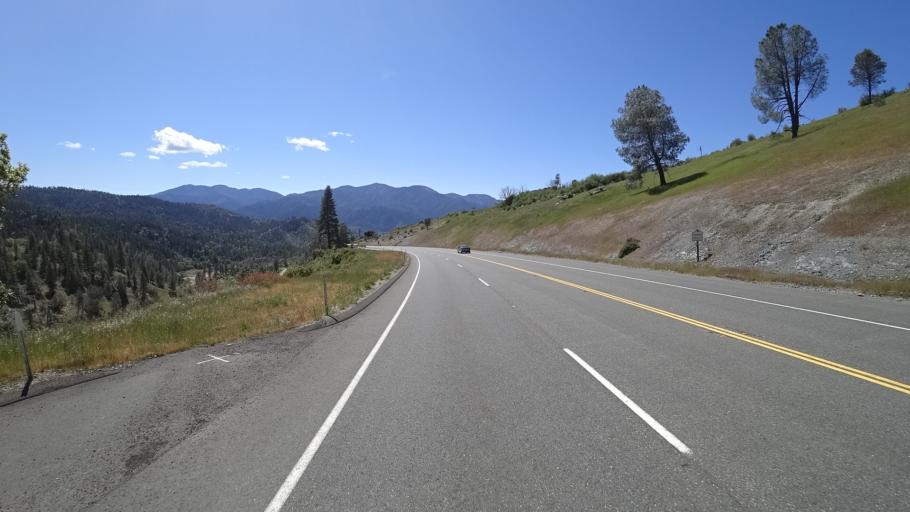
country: US
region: California
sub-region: Trinity County
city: Weaverville
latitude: 40.7393
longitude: -122.9943
